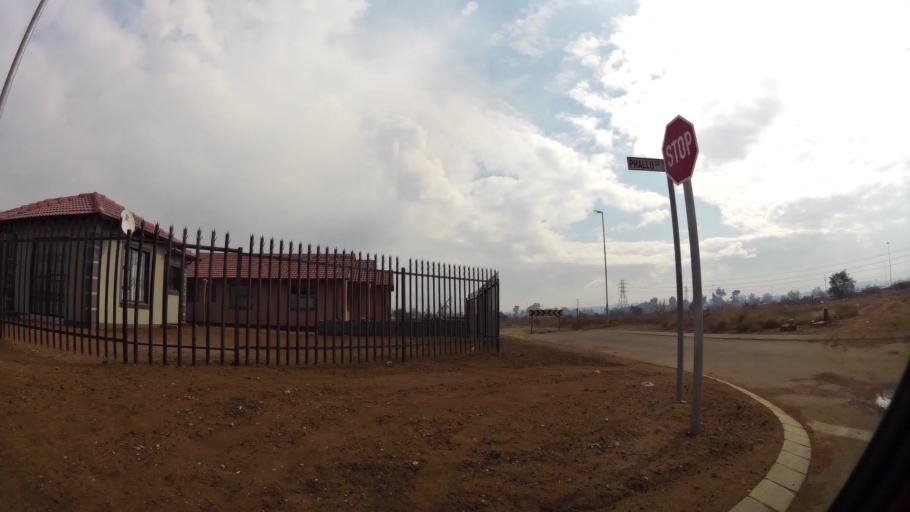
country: ZA
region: Gauteng
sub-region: Sedibeng District Municipality
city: Vanderbijlpark
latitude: -26.6795
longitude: 27.8437
